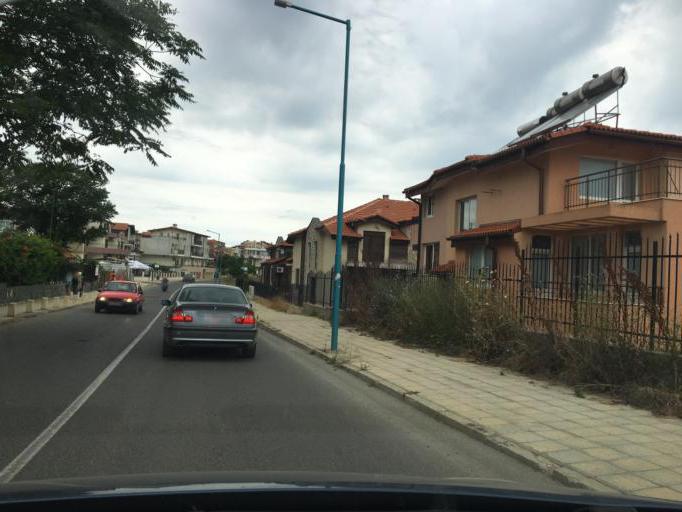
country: BG
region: Burgas
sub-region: Obshtina Sozopol
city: Sozopol
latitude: 42.4078
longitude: 27.7058
